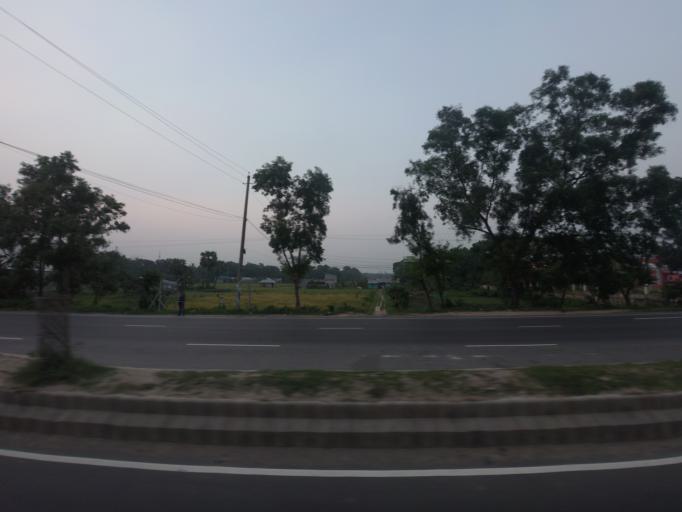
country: BD
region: Chittagong
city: Comilla
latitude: 23.4775
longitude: 91.0995
